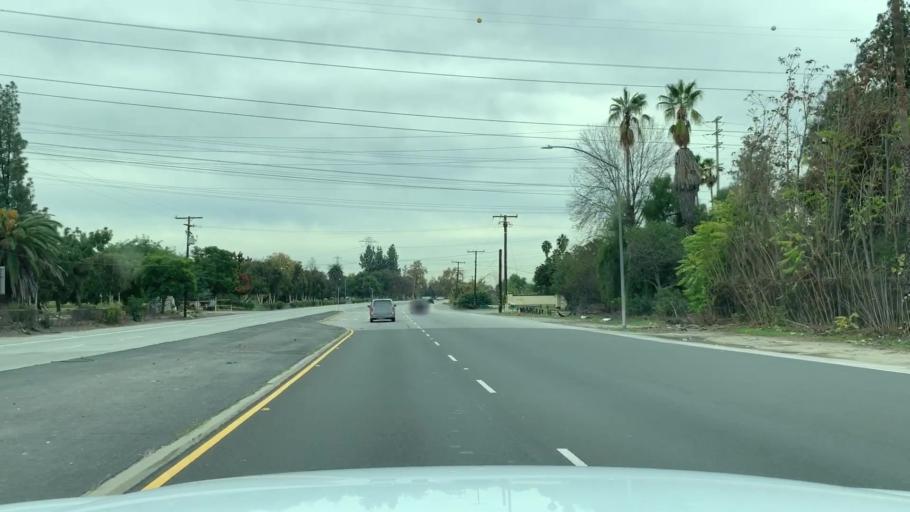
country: US
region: California
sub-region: Los Angeles County
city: South El Monte
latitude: 34.0383
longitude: -118.0644
